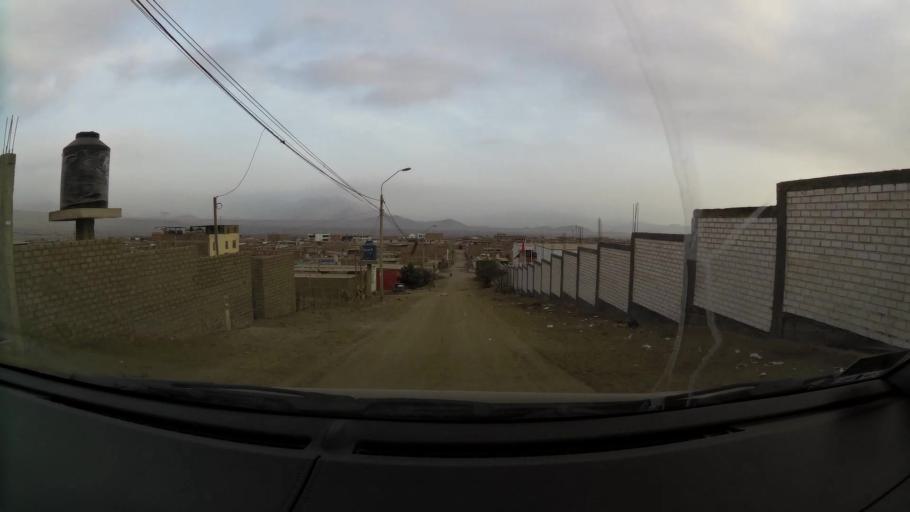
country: PE
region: Lima
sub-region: Lima
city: Santa Rosa
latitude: -11.7297
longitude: -77.1423
